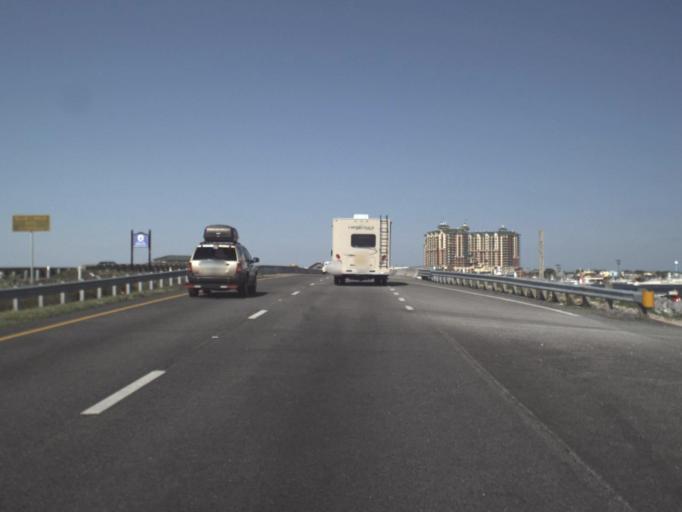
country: US
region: Florida
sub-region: Okaloosa County
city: Destin
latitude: 30.3910
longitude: -86.5234
